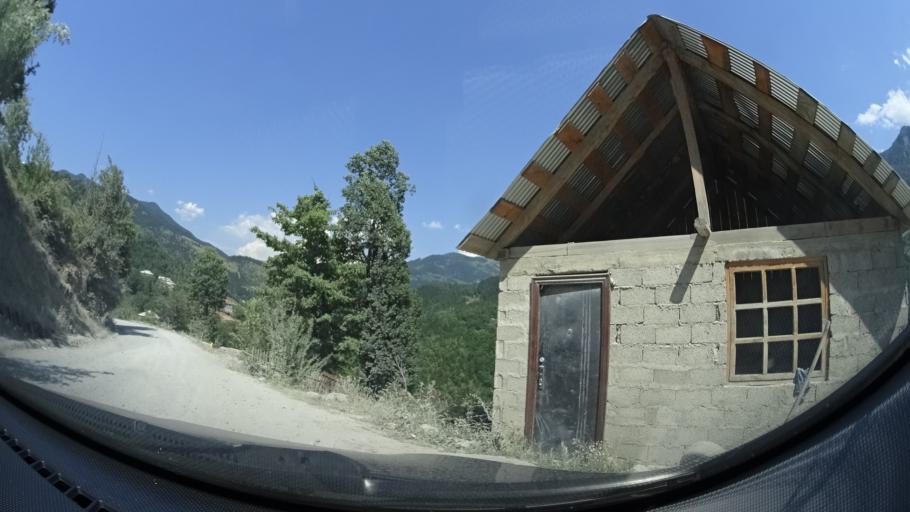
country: GE
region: Ajaria
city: Khulo
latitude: 41.6511
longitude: 42.3232
